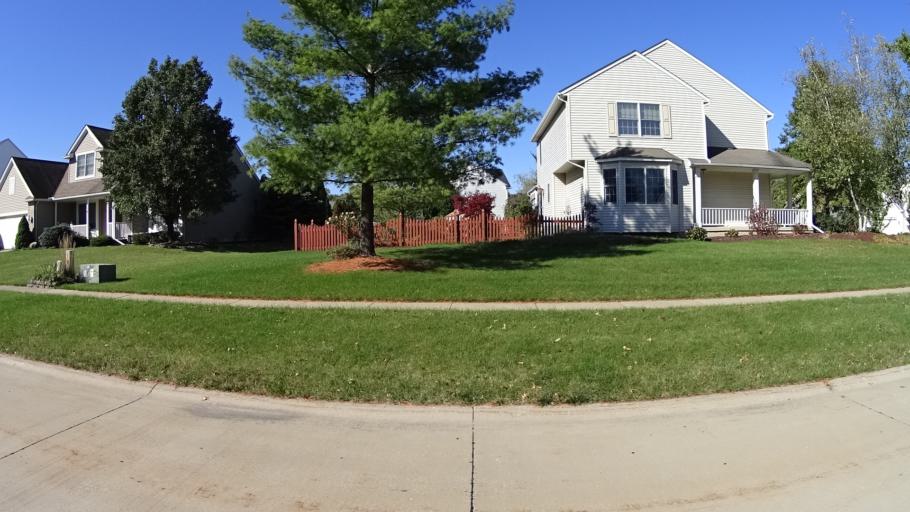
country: US
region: Ohio
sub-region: Lorain County
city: Amherst
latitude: 41.3843
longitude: -82.2455
